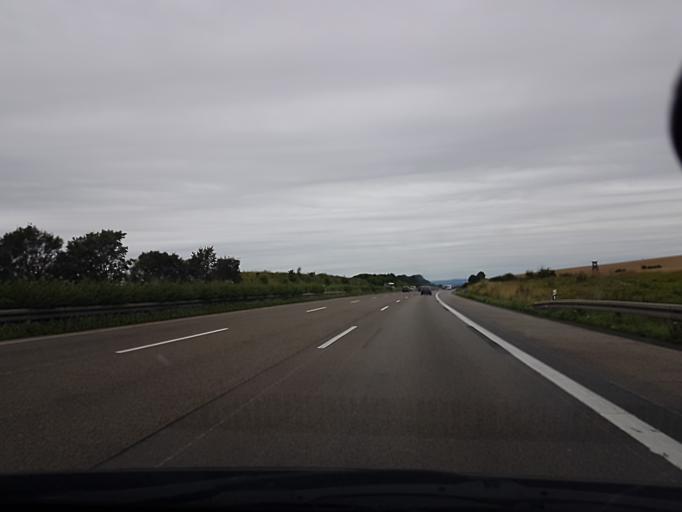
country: DE
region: Hesse
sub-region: Regierungsbezirk Giessen
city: Villmar
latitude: 50.3416
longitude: 8.1783
